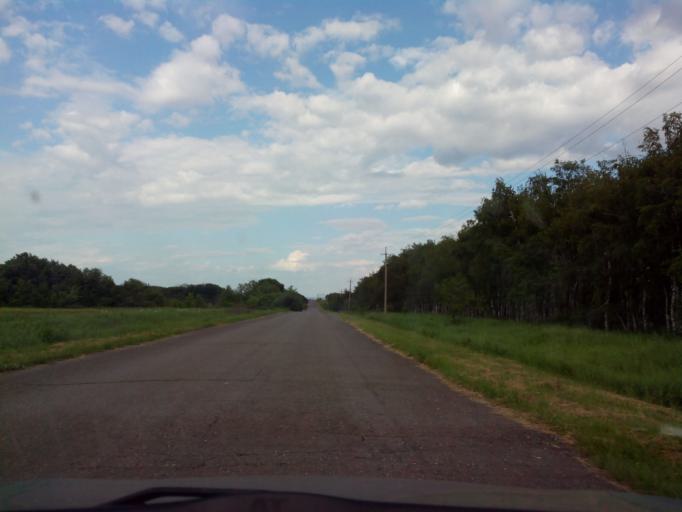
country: RU
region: Volgograd
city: Slashchevskaya
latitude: 49.7948
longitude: 42.3952
